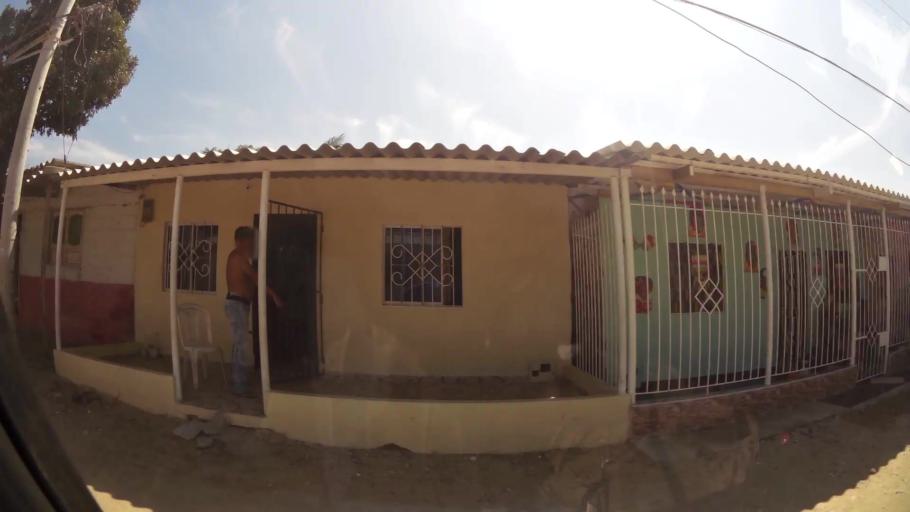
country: CO
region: Atlantico
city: Barranquilla
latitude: 10.9759
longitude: -74.8452
